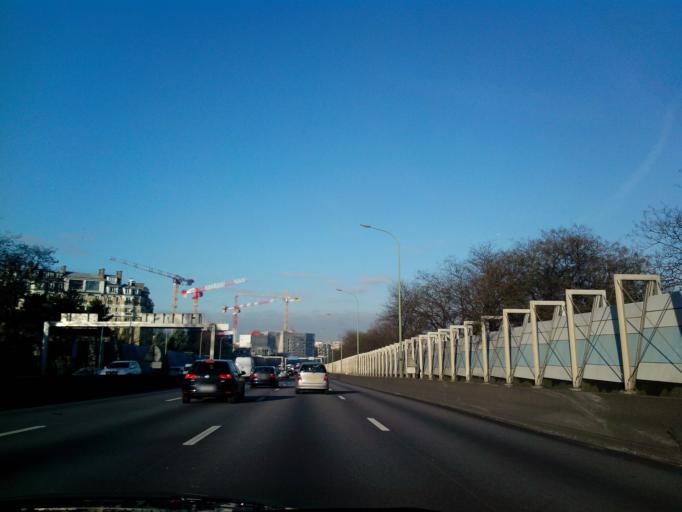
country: FR
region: Ile-de-France
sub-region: Departement de Seine-Saint-Denis
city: Le Pre-Saint-Gervais
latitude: 48.8825
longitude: 2.4012
